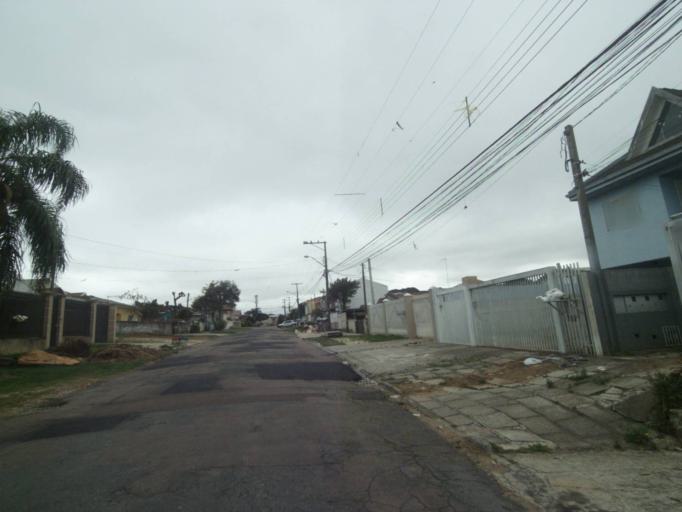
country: BR
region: Parana
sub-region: Sao Jose Dos Pinhais
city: Sao Jose dos Pinhais
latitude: -25.5397
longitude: -49.2886
